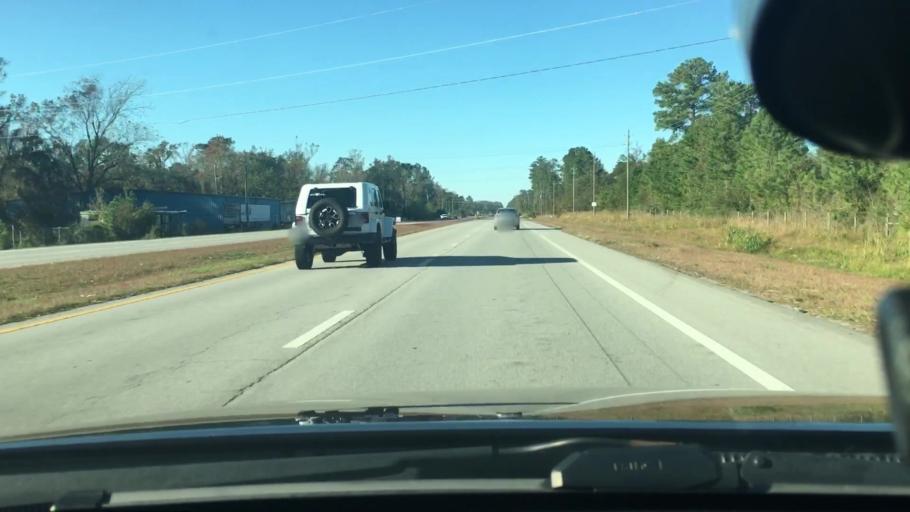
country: US
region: North Carolina
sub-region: Craven County
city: New Bern
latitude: 35.1423
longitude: -77.0300
